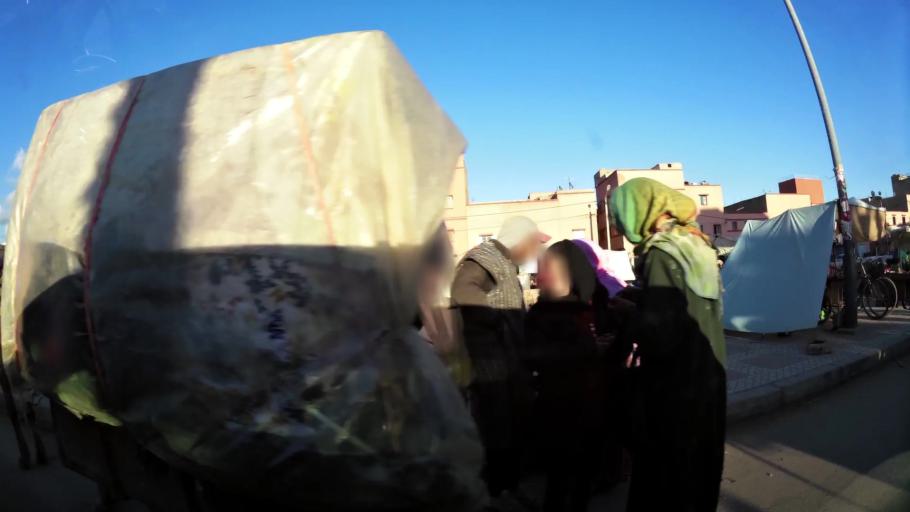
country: MA
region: Marrakech-Tensift-Al Haouz
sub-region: Kelaa-Des-Sraghna
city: Sidi Abdallah
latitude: 32.2437
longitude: -7.9487
